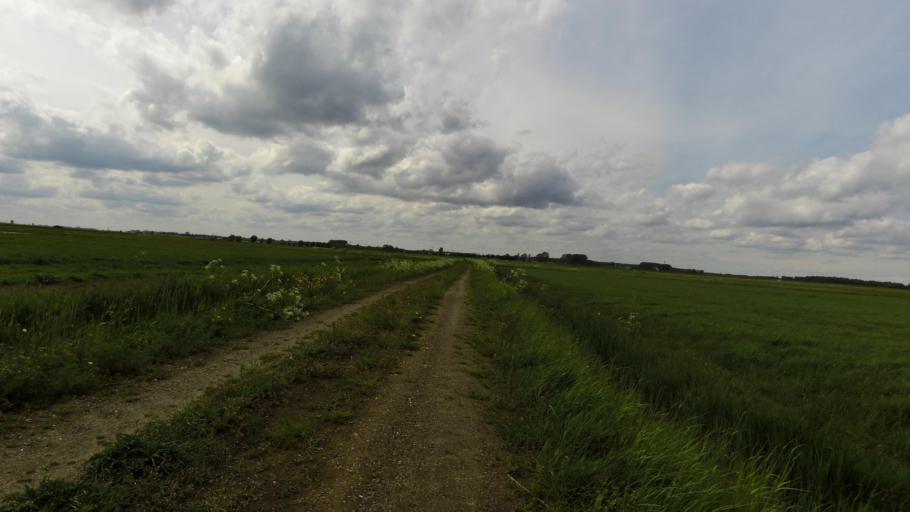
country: NL
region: Gelderland
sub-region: Gemeente Nijkerk
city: Nijkerk
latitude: 52.2489
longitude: 5.4827
